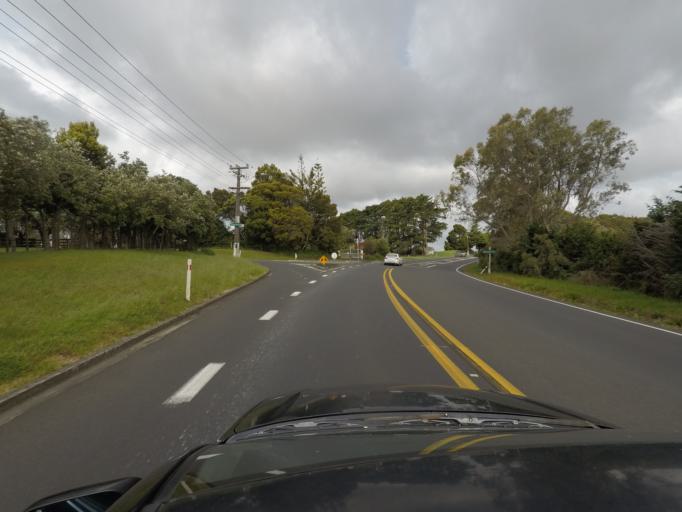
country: NZ
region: Auckland
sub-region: Auckland
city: Pakuranga
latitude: -36.9374
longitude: 174.9456
